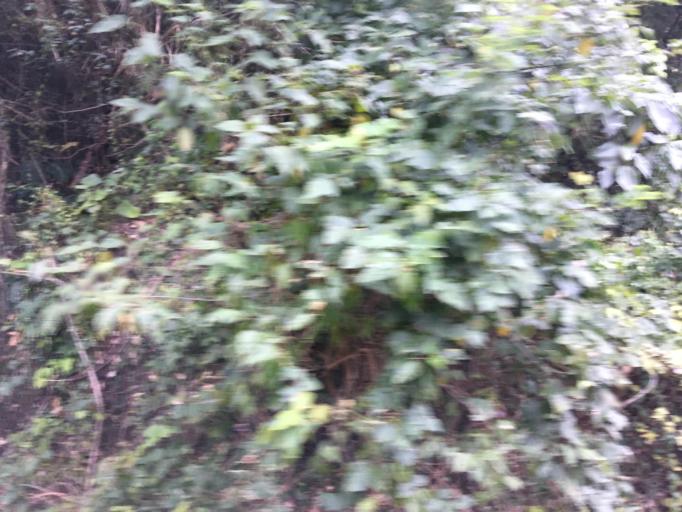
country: TW
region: Taiwan
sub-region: Chiayi
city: Jiayi Shi
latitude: 23.5340
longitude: 120.6035
